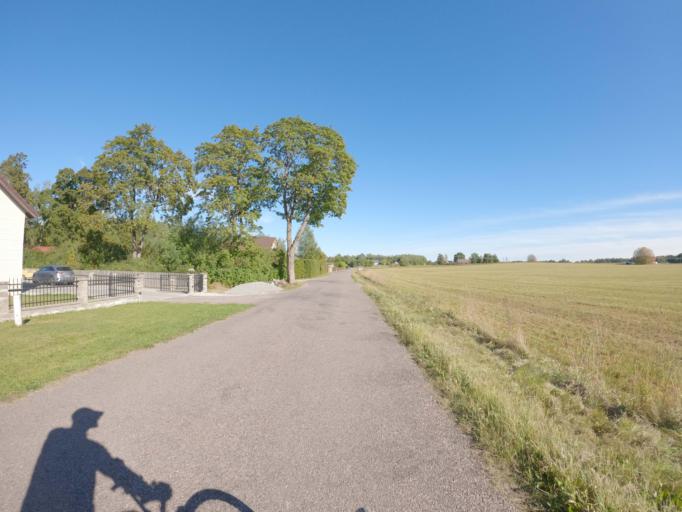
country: EE
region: Raplamaa
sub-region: Rapla vald
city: Rapla
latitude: 58.9878
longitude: 24.8170
